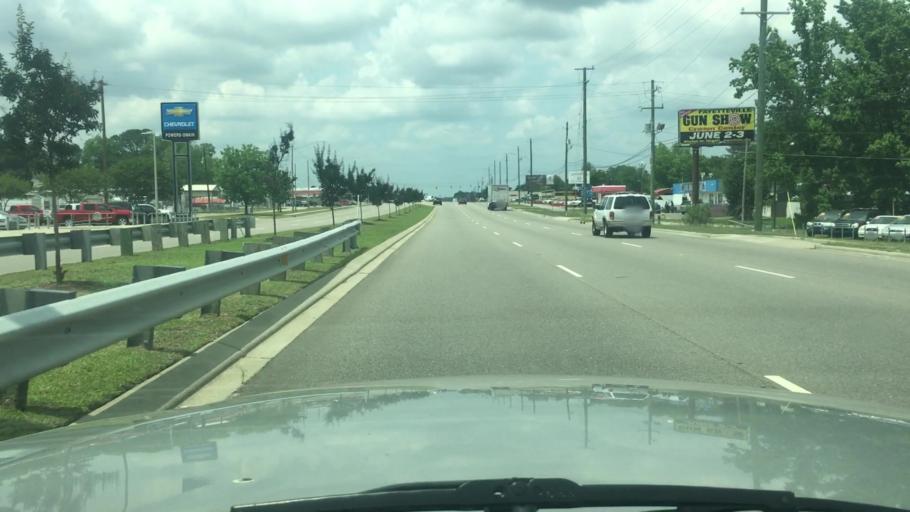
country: US
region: North Carolina
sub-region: Cumberland County
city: Fort Bragg
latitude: 35.0903
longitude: -78.9539
